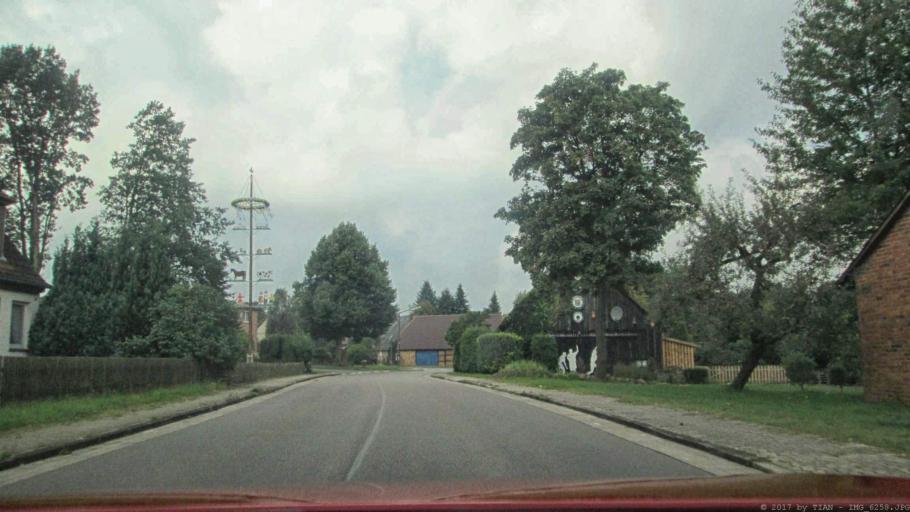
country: DE
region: Lower Saxony
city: Hankensbuttel
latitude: 52.6843
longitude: 10.5749
